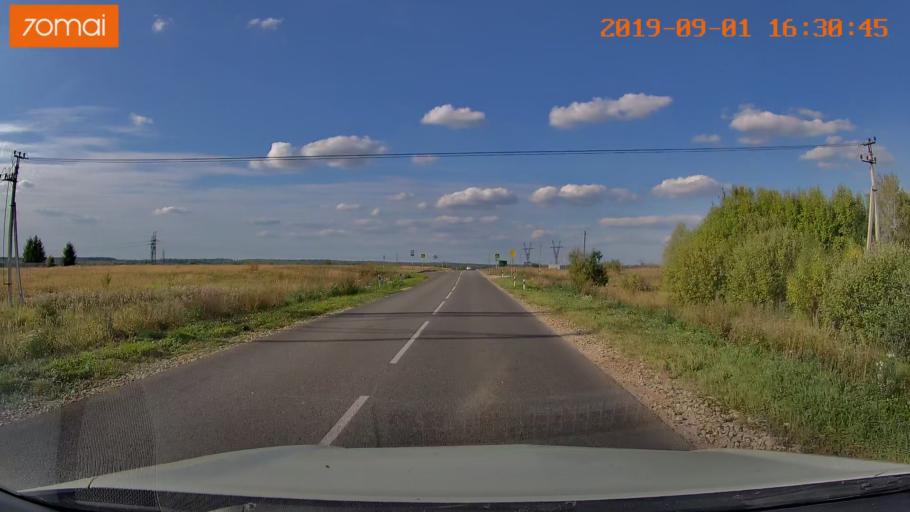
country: RU
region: Kaluga
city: Maloyaroslavets
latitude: 54.9485
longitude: 36.4586
